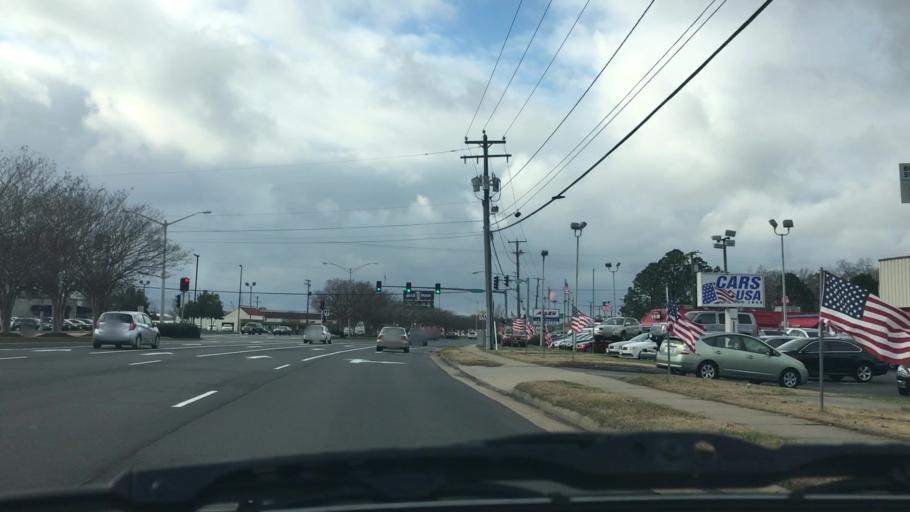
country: US
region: Virginia
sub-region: City of Chesapeake
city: Chesapeake
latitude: 36.8440
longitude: -76.1511
